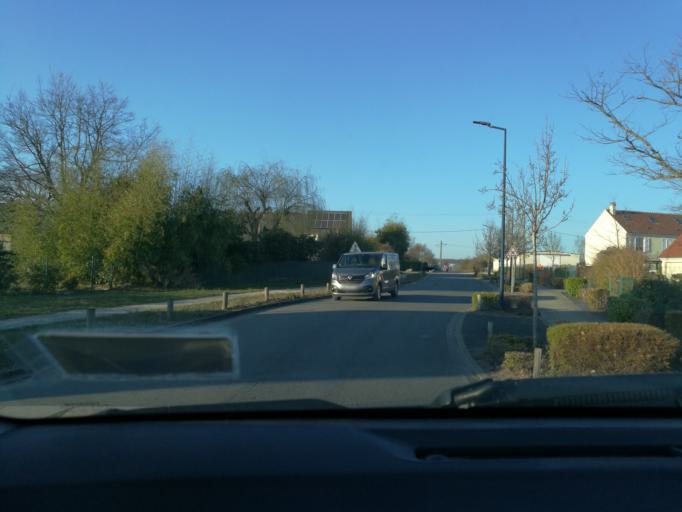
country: FR
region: Centre
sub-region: Departement du Loiret
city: Semoy
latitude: 47.9353
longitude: 1.9524
